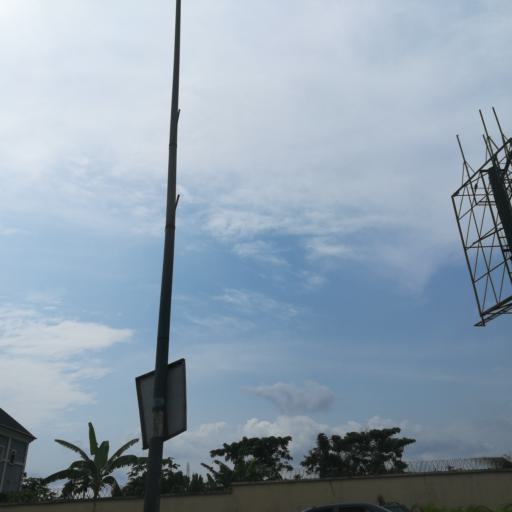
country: NG
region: Rivers
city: Port Harcourt
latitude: 4.8406
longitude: 7.0148
